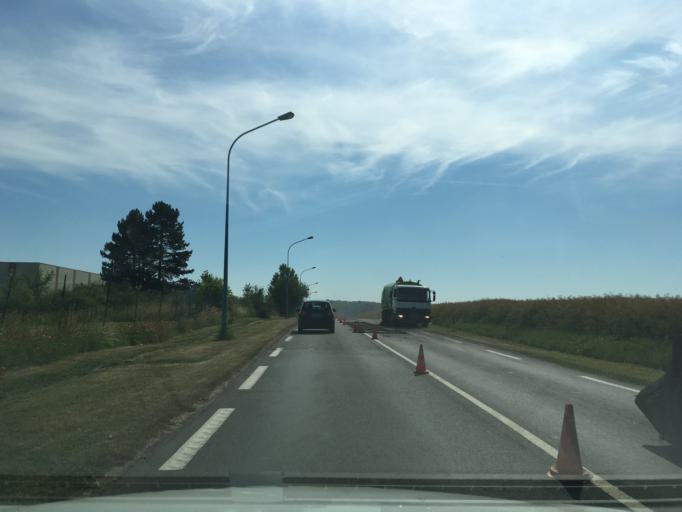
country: FR
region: Picardie
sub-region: Departement de la Somme
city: Montdidier
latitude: 49.6476
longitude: 2.5926
